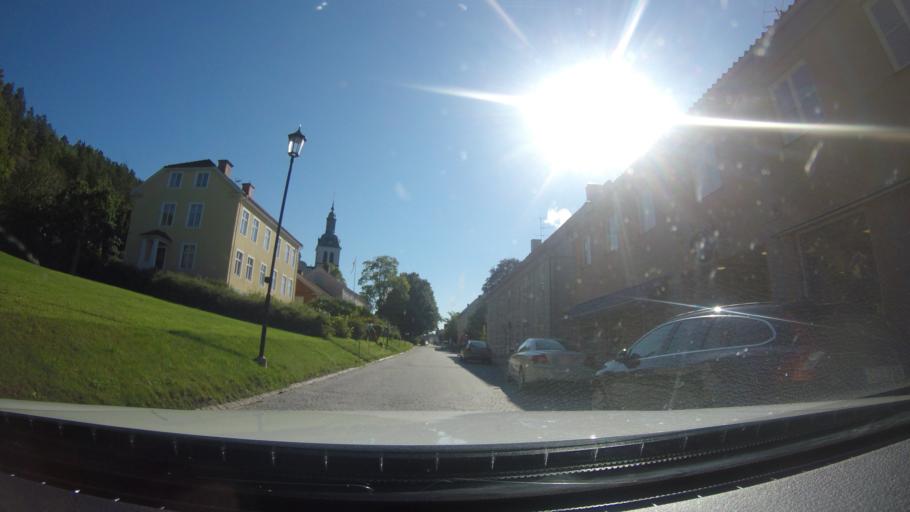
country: SE
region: Joenkoeping
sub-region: Jonkopings Kommun
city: Graenna
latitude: 58.0216
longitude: 14.4661
